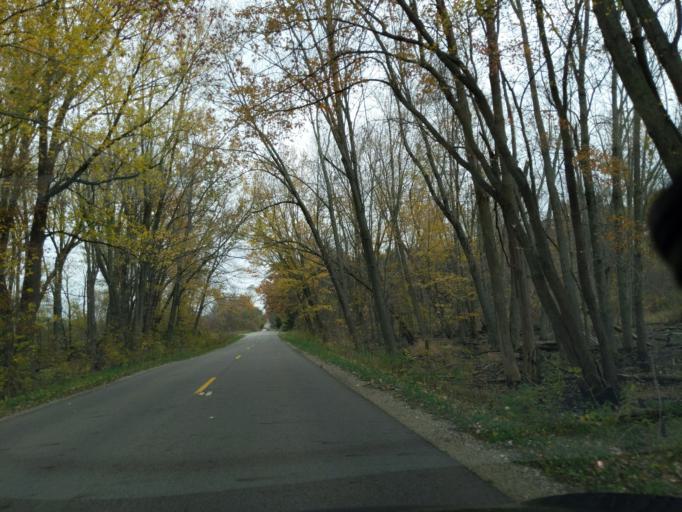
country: US
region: Michigan
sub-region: Eaton County
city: Eaton Rapids
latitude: 42.5240
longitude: -84.6117
